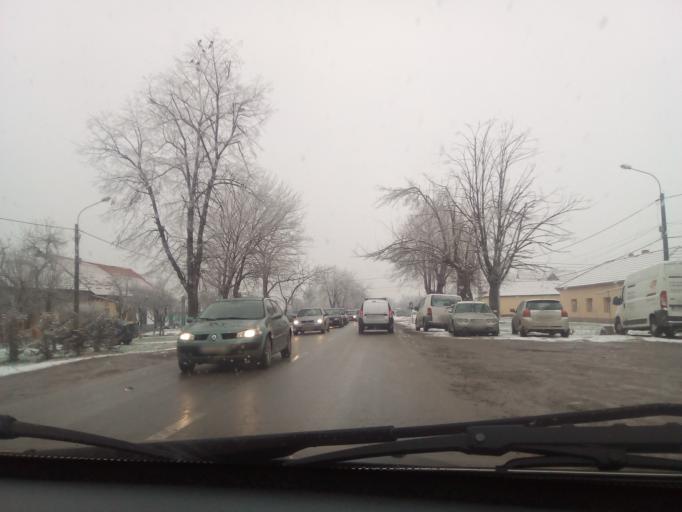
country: RO
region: Timis
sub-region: Comuna Mosnita Noua
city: Mosnita Noua
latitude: 45.7185
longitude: 21.3251
